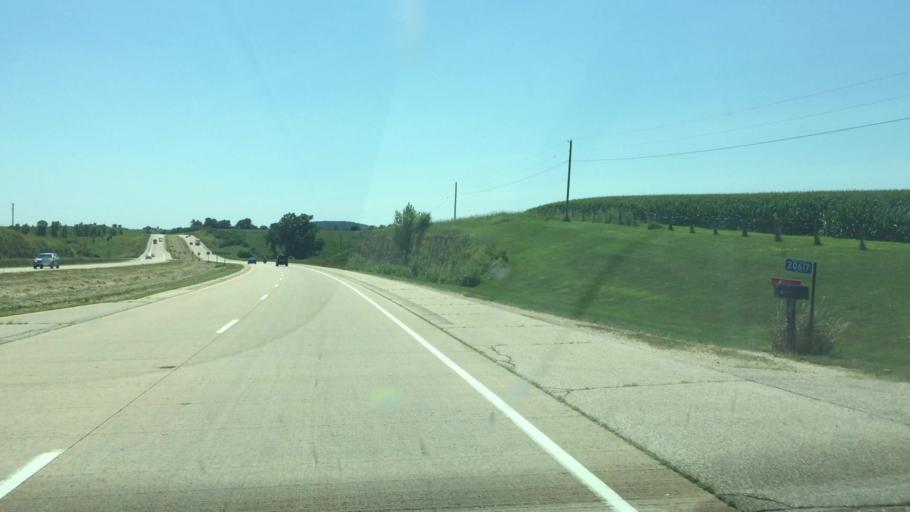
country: US
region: Wisconsin
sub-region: Iowa County
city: Mineral Point
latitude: 42.7939
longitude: -90.2878
